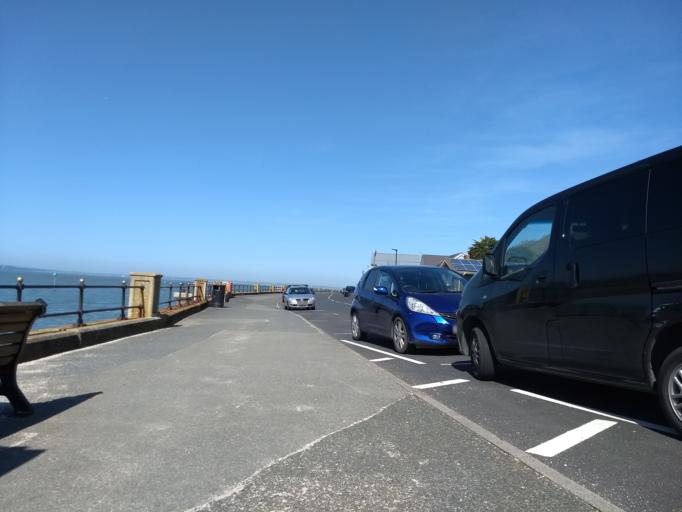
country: GB
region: England
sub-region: Isle of Wight
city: Gurnard
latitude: 50.7625
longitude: -1.3239
